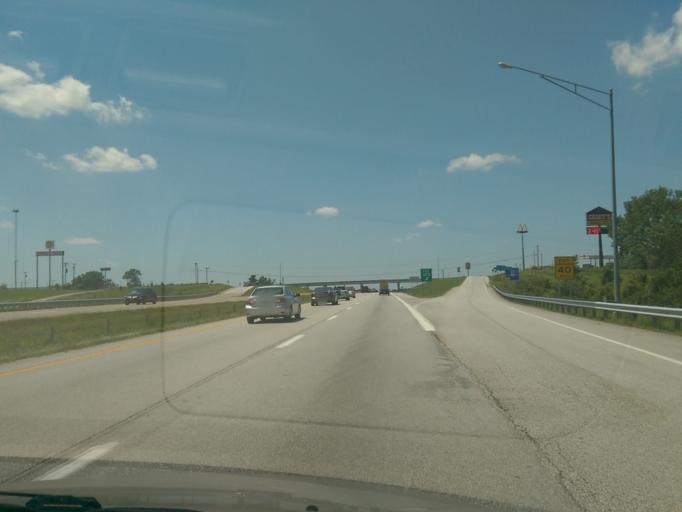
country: US
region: Missouri
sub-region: Cooper County
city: Boonville
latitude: 38.9367
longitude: -92.7399
